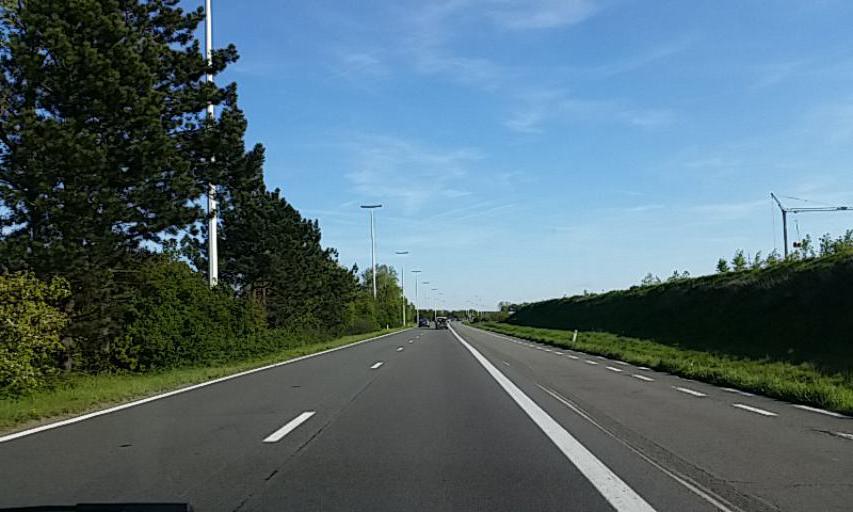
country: BE
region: Flanders
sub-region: Provincie Oost-Vlaanderen
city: Zelzate
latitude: 51.2021
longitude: 3.8252
